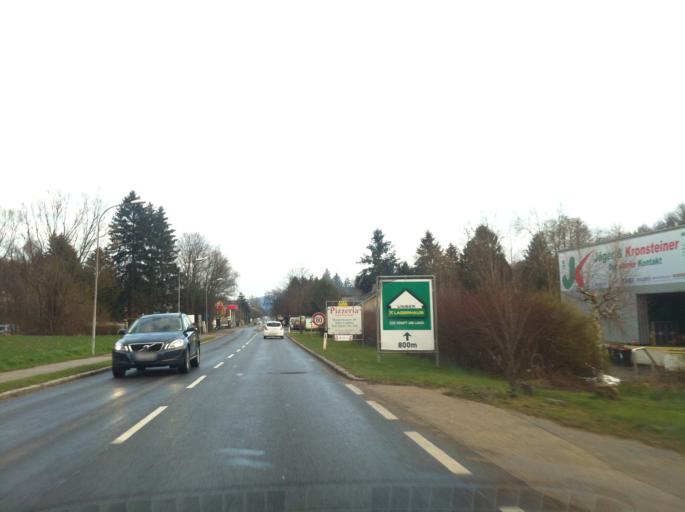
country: AT
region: Lower Austria
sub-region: Politischer Bezirk Wien-Umgebung
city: Gablitz
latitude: 48.2401
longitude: 16.1354
